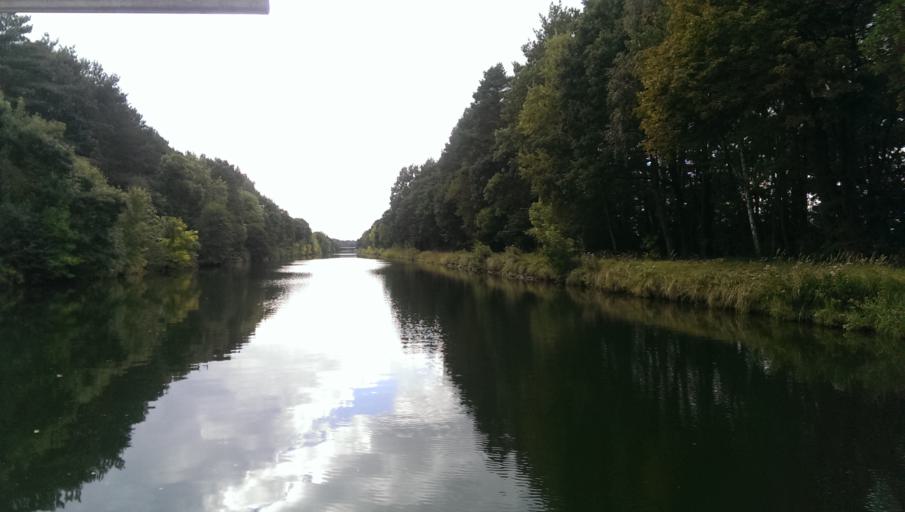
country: DE
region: Brandenburg
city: Marienwerder
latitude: 52.8479
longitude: 13.5632
